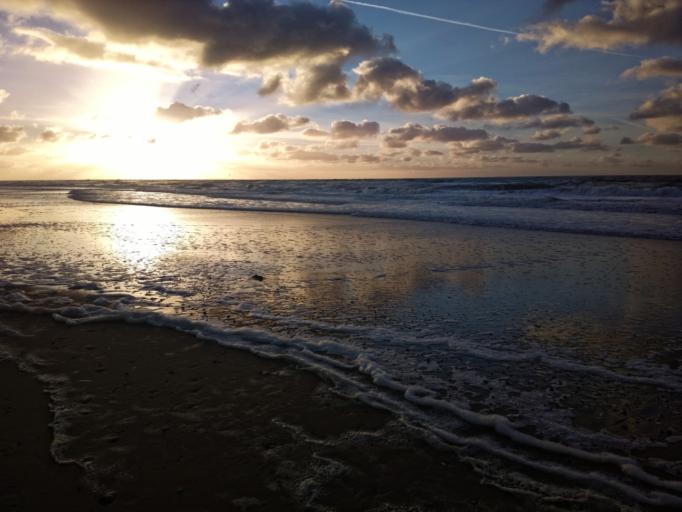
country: NL
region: North Holland
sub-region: Gemeente Texel
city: Den Burg
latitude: 53.0811
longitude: 4.7346
